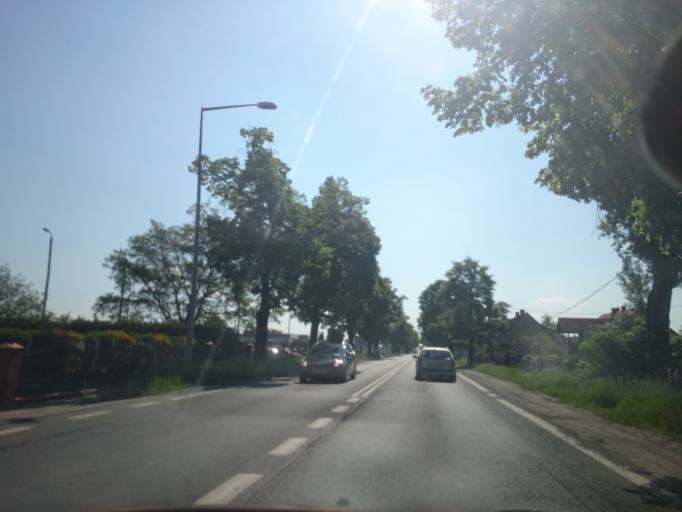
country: PL
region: Opole Voivodeship
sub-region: Powiat opolski
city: Opole
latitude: 50.6539
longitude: 17.9581
